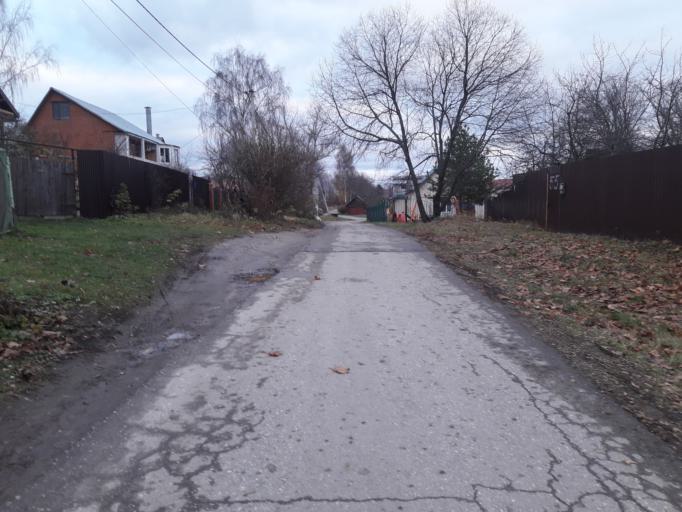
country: RU
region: Moskovskaya
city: Ashukino
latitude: 56.1745
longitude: 37.9338
